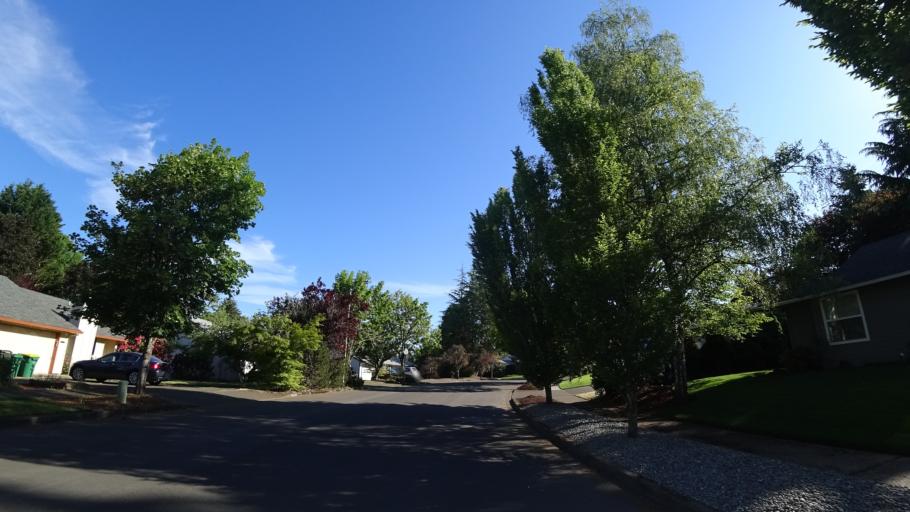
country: US
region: Oregon
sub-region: Washington County
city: Beaverton
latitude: 45.4577
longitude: -122.8111
